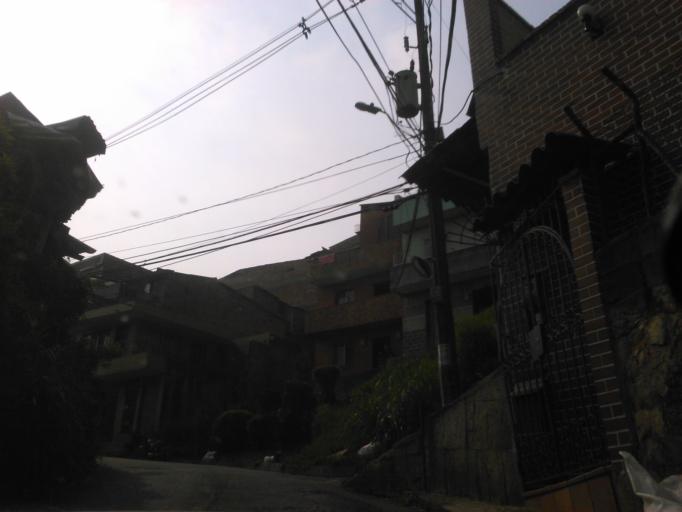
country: CO
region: Antioquia
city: La Estrella
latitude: 6.1480
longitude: -75.6362
